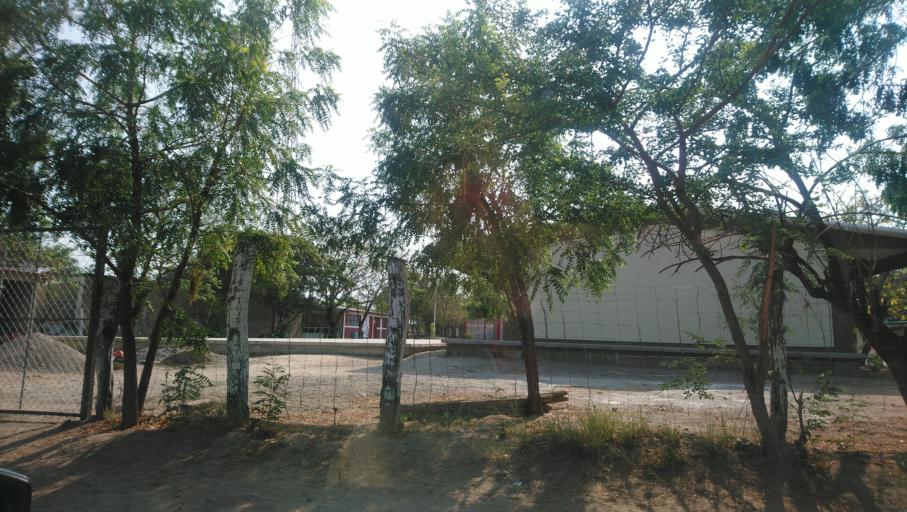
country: MX
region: Oaxaca
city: San Jeronimo Ixtepec
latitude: 16.5589
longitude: -95.1002
